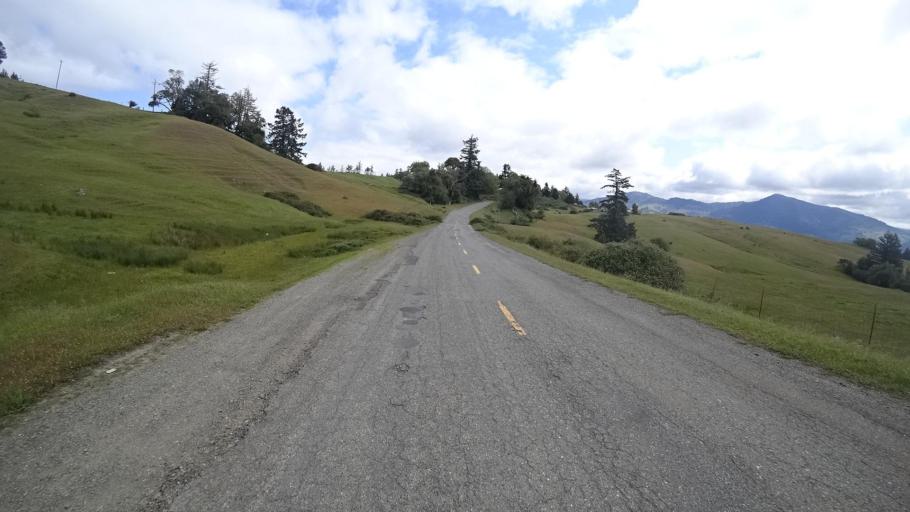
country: US
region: California
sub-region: Humboldt County
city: Redway
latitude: 40.1317
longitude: -123.6302
